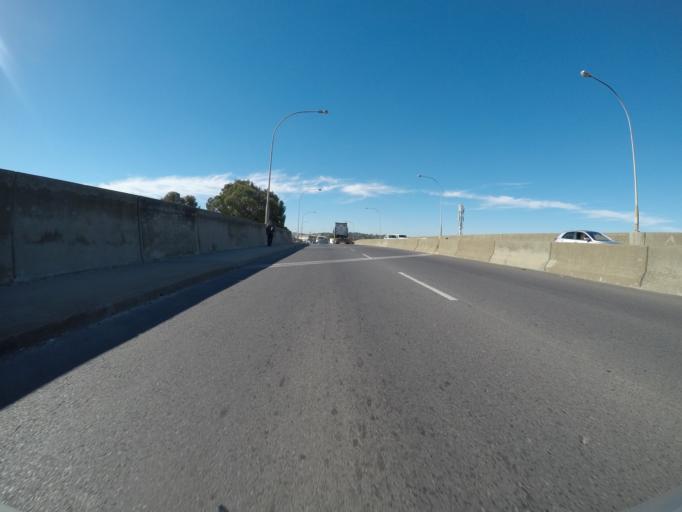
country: ZA
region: Western Cape
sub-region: City of Cape Town
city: Kraaifontein
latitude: -33.8931
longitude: 18.6725
